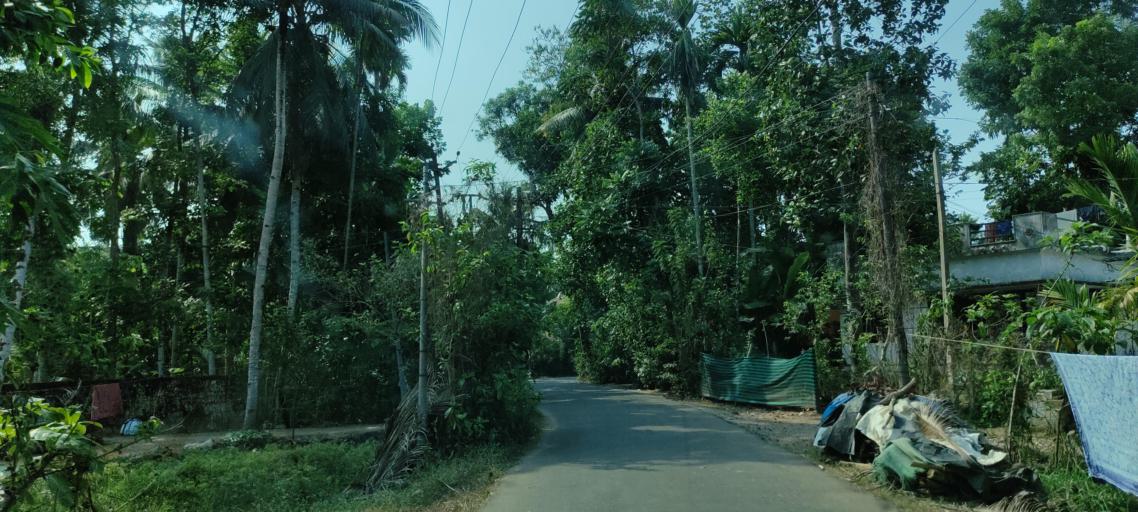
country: IN
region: Kerala
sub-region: Pattanamtitta
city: Tiruvalla
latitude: 9.3562
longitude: 76.5155
